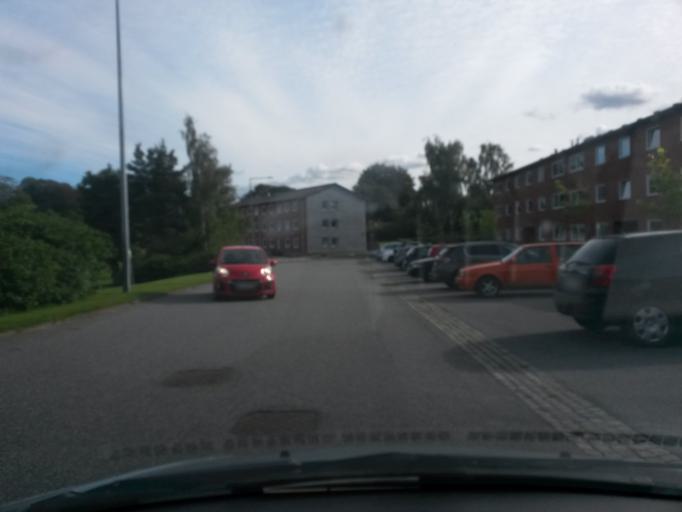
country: DK
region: Central Jutland
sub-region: Silkeborg Kommune
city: Kjellerup
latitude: 56.2924
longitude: 9.4328
